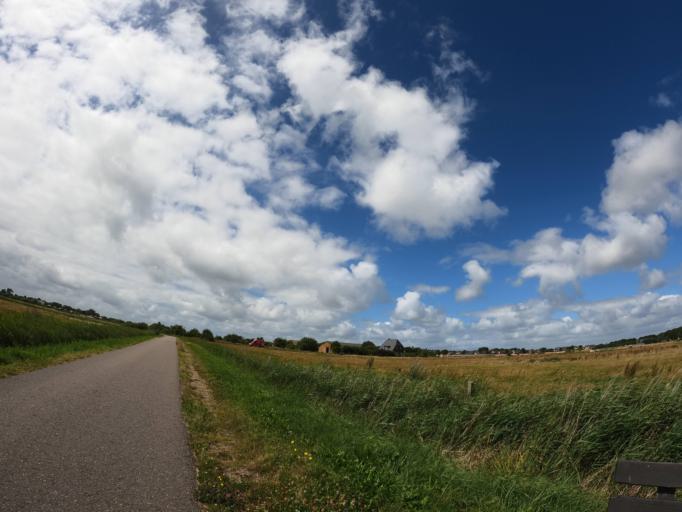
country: DE
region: Schleswig-Holstein
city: Tinnum
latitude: 54.8913
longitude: 8.3381
